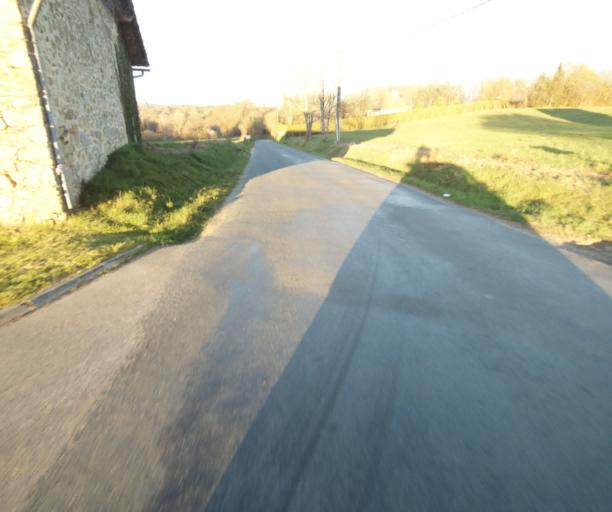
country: FR
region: Limousin
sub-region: Departement de la Correze
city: Saint-Clement
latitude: 45.3223
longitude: 1.6694
